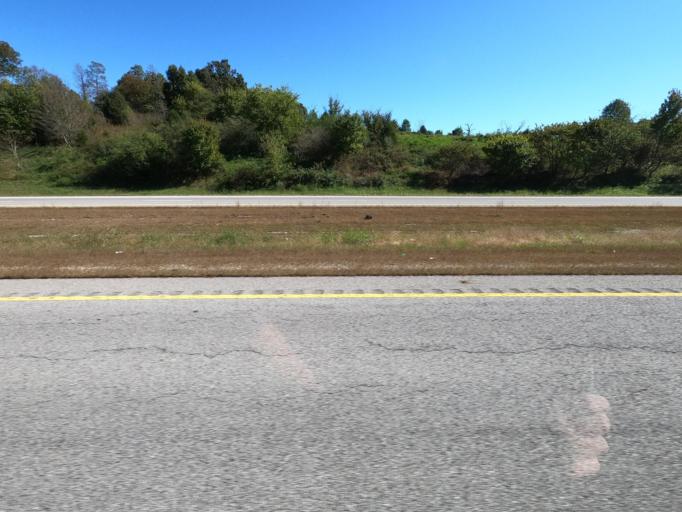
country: US
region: Tennessee
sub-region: Maury County
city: Mount Pleasant
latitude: 35.4666
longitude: -87.2661
